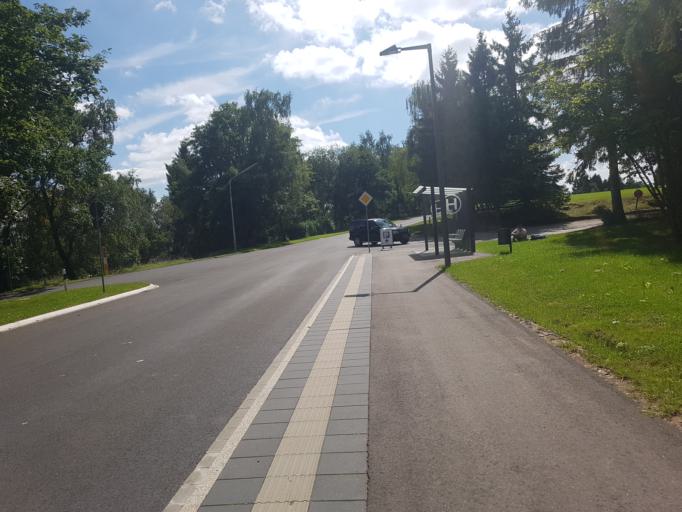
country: DE
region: North Rhine-Westphalia
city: Heimbach
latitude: 50.5853
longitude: 6.4496
